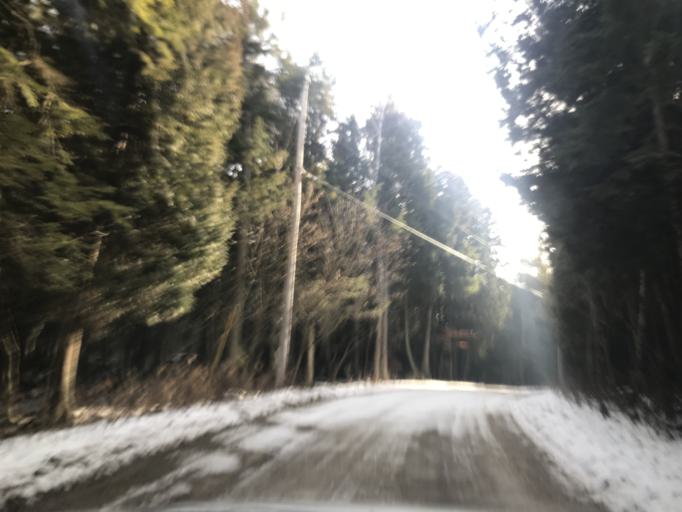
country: US
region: Wisconsin
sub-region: Door County
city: Sturgeon Bay
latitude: 45.1513
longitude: -87.0390
